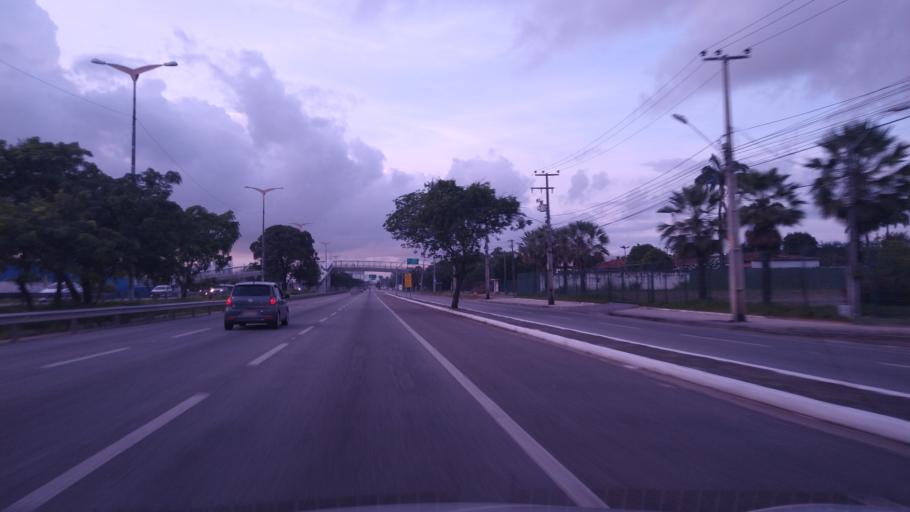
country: BR
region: Ceara
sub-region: Fortaleza
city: Fortaleza
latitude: -3.7919
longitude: -38.5091
